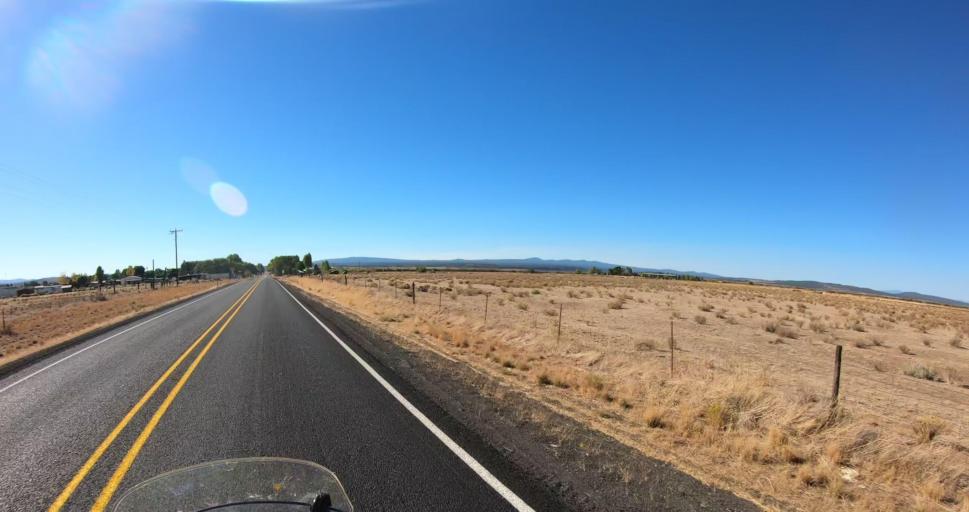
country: US
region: Oregon
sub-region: Deschutes County
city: La Pine
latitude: 43.1281
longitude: -121.0405
